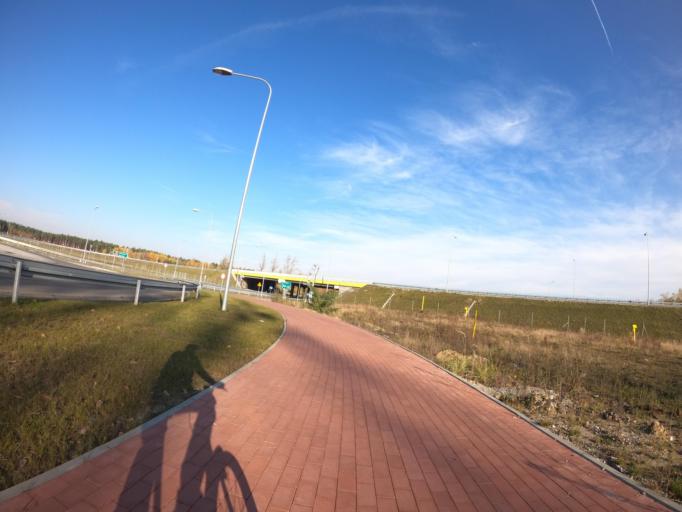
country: PL
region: West Pomeranian Voivodeship
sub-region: Powiat walecki
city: Walcz
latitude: 53.2846
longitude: 16.5051
